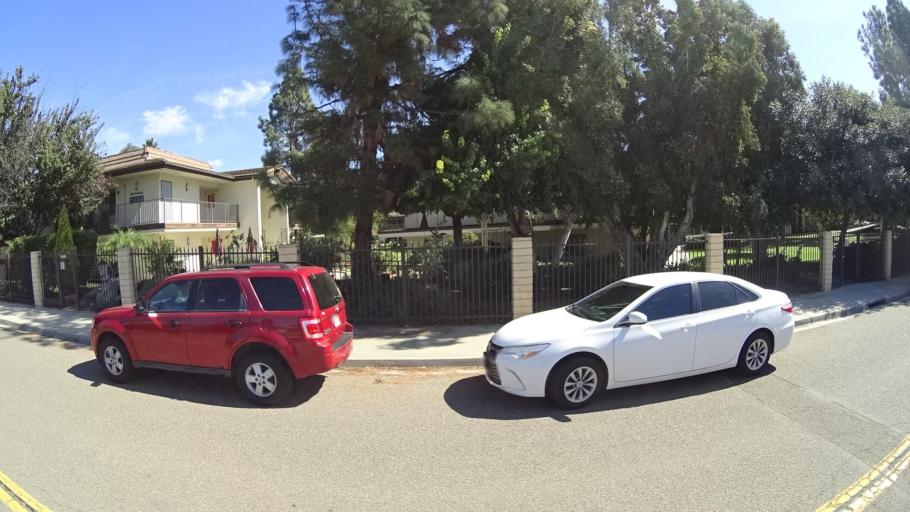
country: US
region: California
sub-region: San Diego County
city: La Presa
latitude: 32.7016
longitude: -117.0021
